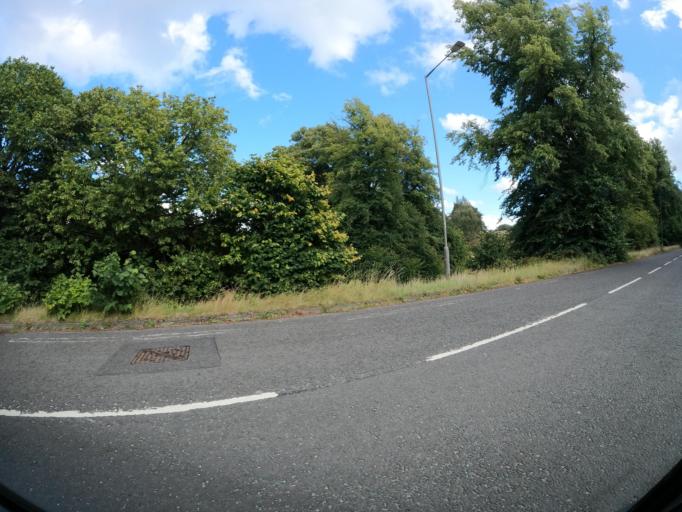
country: GB
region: Scotland
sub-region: Falkirk
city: Falkirk
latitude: 55.9953
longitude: -3.7580
